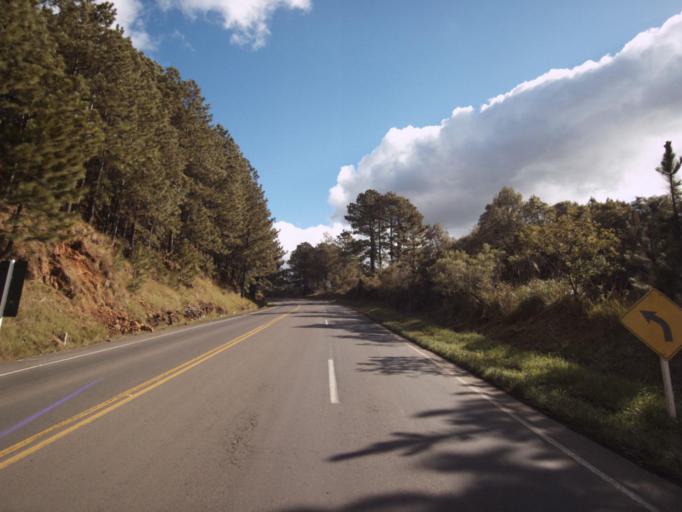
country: BR
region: Santa Catarina
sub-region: Joacaba
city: Joacaba
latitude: -27.0205
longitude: -51.7309
